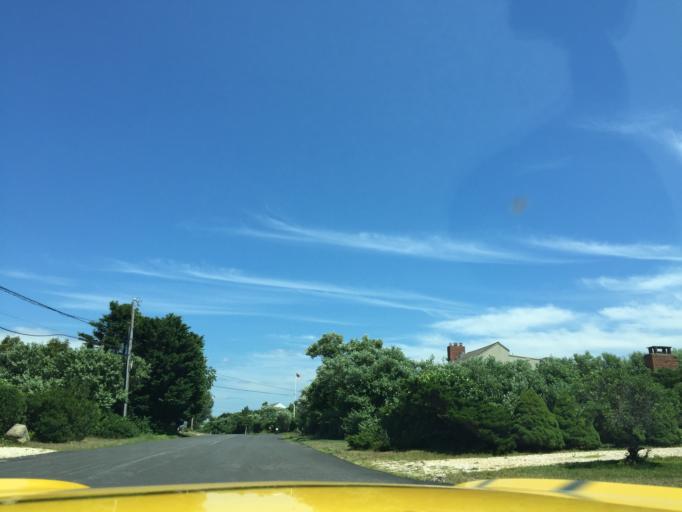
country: US
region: New York
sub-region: Suffolk County
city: Montauk
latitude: 41.0719
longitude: -71.9505
